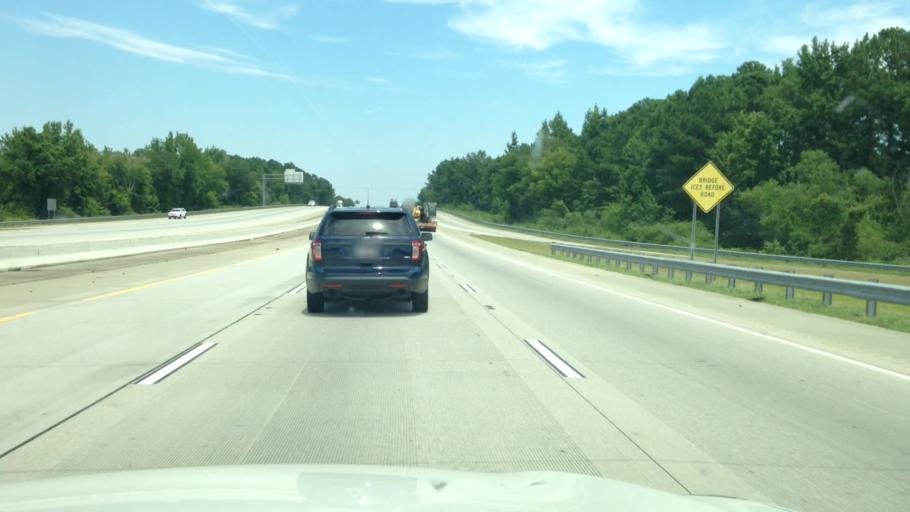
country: US
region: South Carolina
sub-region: Florence County
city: Florence
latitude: 34.2314
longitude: -79.7970
